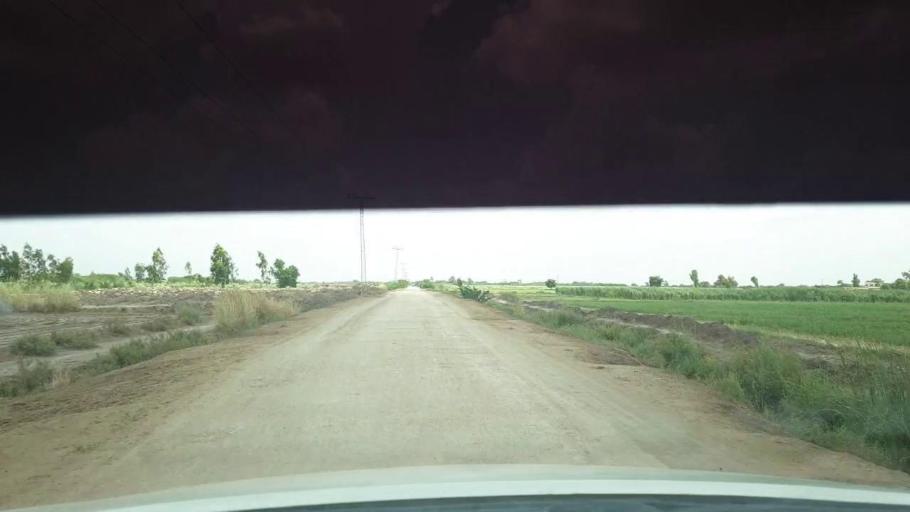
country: PK
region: Sindh
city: Kadhan
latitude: 24.4651
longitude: 68.9974
